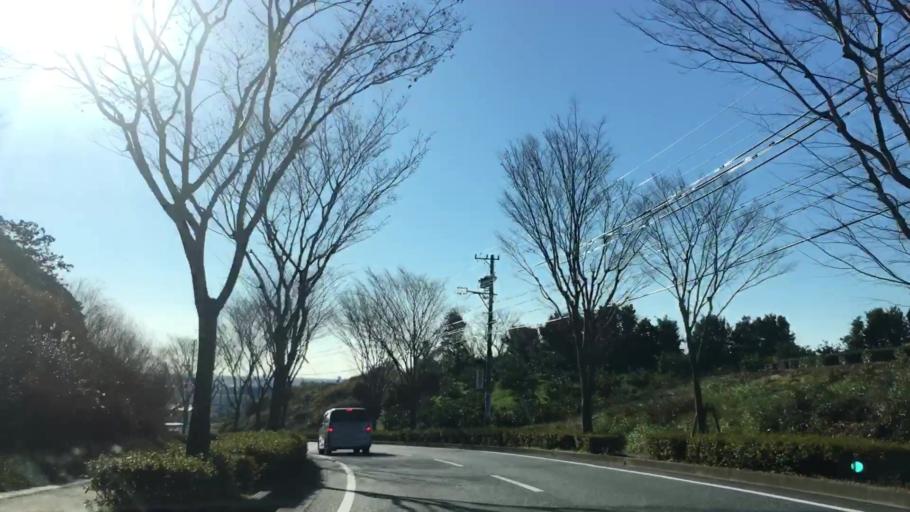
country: JP
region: Shizuoka
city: Hamakita
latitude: 34.8019
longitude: 137.7451
